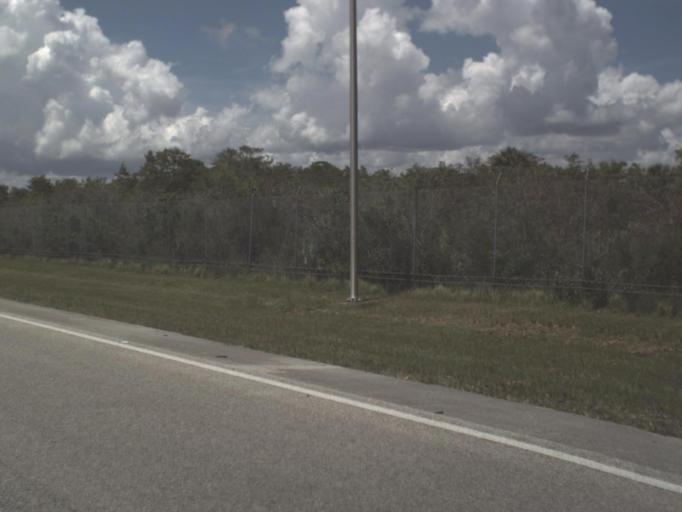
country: US
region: Florida
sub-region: Collier County
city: Immokalee
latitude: 26.1672
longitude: -81.2022
